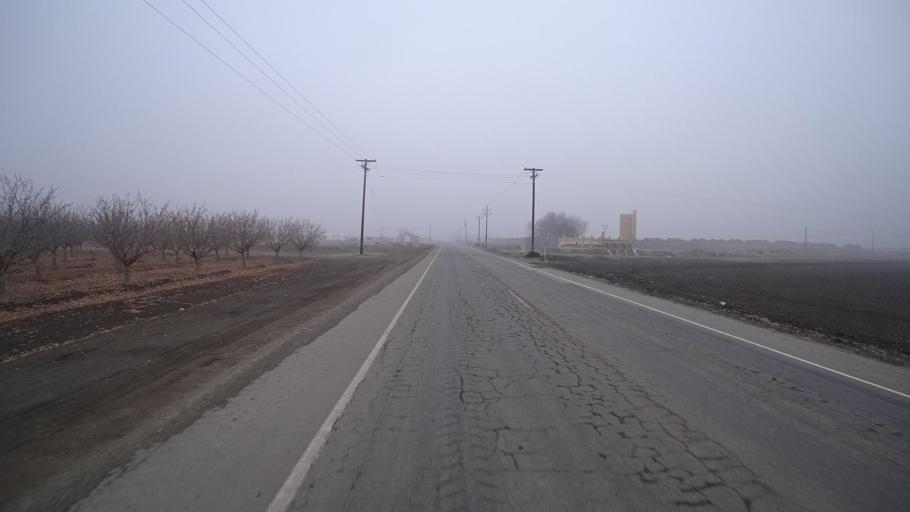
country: US
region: California
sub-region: Kern County
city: Buttonwillow
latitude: 35.4060
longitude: -119.5185
